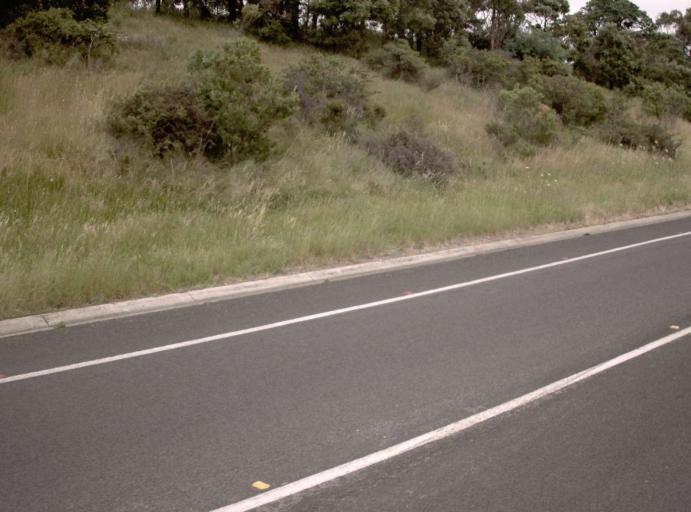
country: AU
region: Victoria
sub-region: Cardinia
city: Bunyip
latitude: -38.0892
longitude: 145.8040
